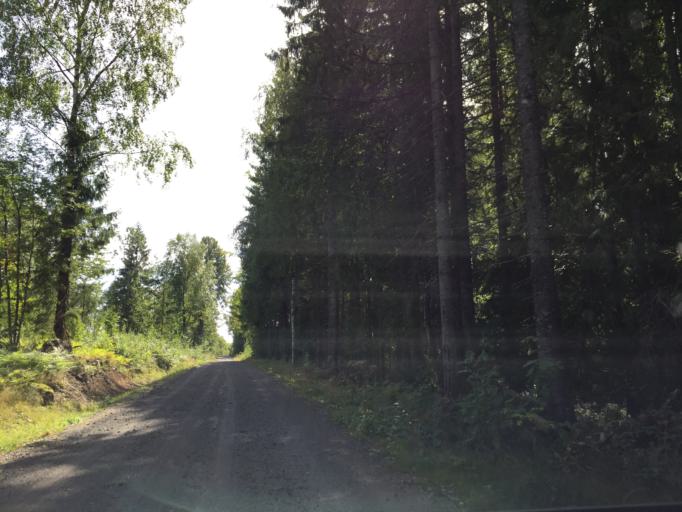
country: NO
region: Vestfold
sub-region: Hof
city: Hof
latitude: 59.4463
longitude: 10.1561
